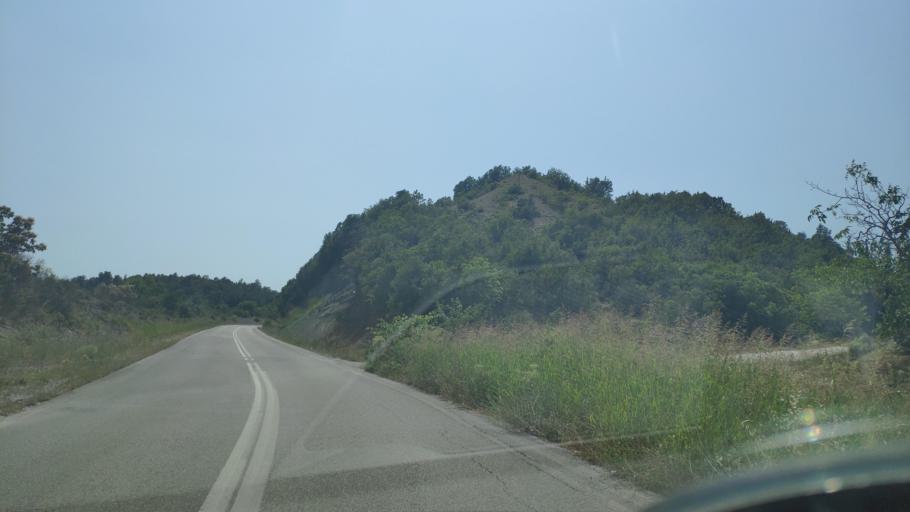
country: GR
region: Epirus
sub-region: Nomos Artas
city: Ano Kalentini
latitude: 39.2209
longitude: 21.1408
